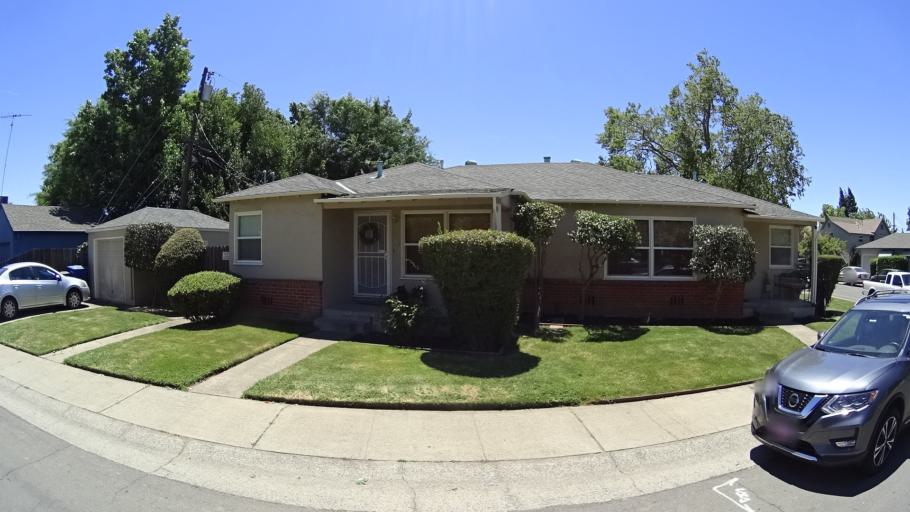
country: US
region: California
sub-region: Sacramento County
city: Sacramento
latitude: 38.5705
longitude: -121.4351
